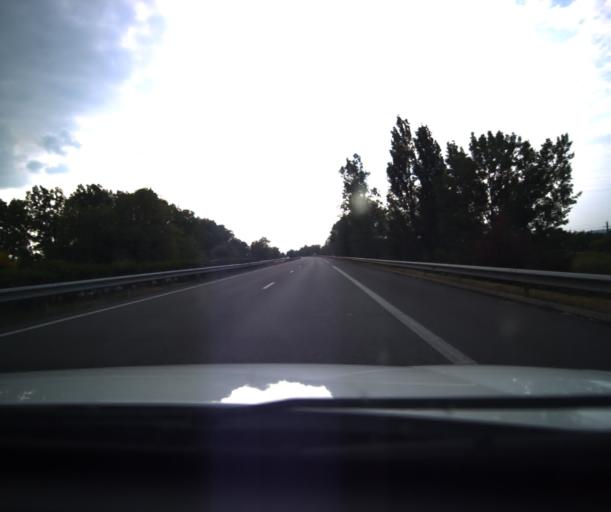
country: FR
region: Midi-Pyrenees
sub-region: Departement du Tarn-et-Garonne
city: Castelsarrasin
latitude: 44.0557
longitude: 1.1226
